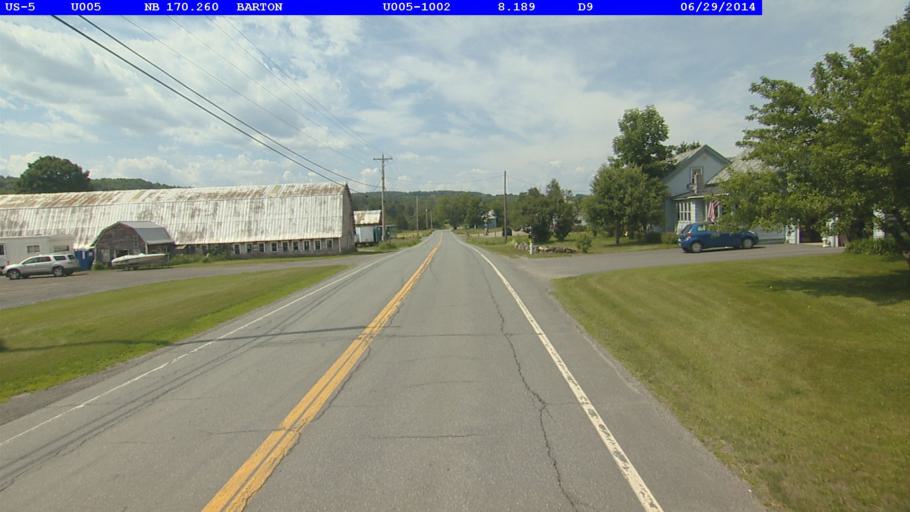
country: US
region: Vermont
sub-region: Orleans County
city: Newport
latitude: 44.7759
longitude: -72.2112
